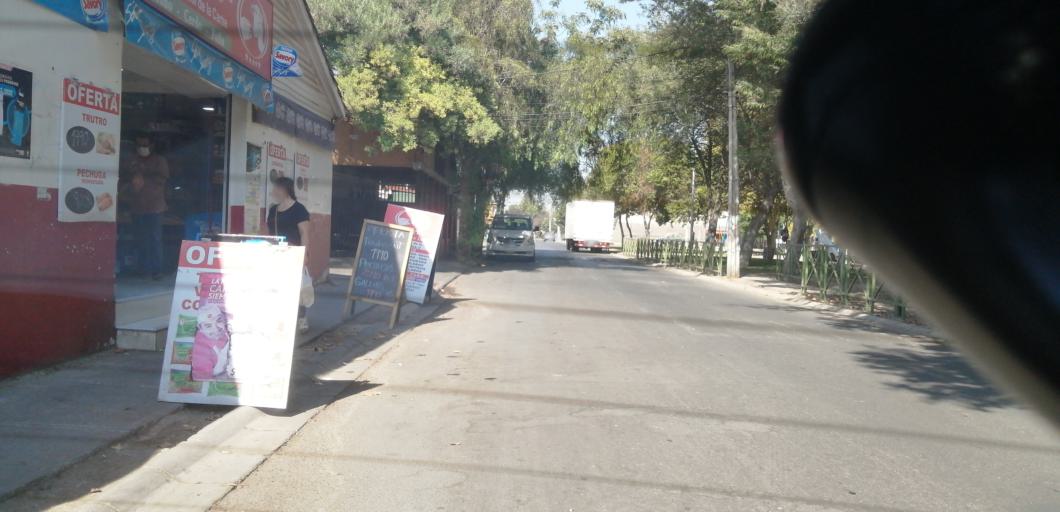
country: CL
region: Santiago Metropolitan
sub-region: Provincia de Santiago
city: Lo Prado
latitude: -33.4532
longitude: -70.7465
